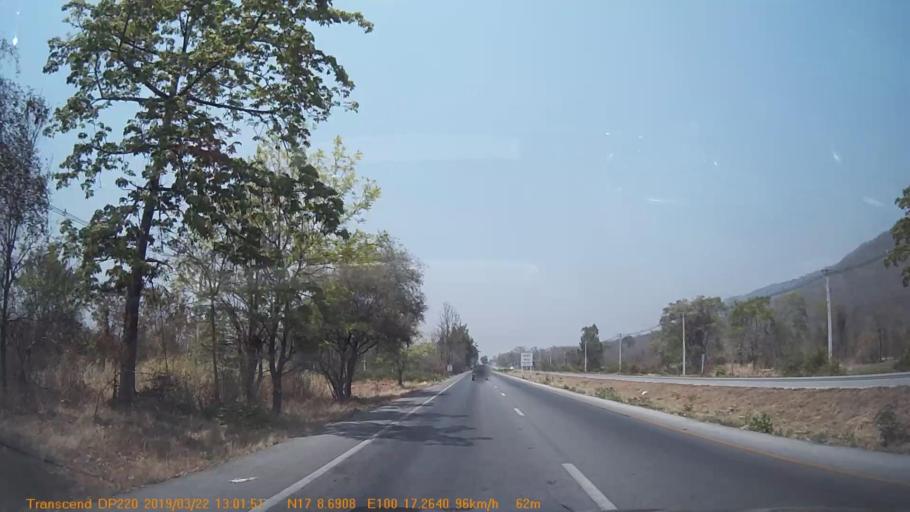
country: TH
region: Phitsanulok
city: Phrom Phiram
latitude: 17.1451
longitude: 100.2876
